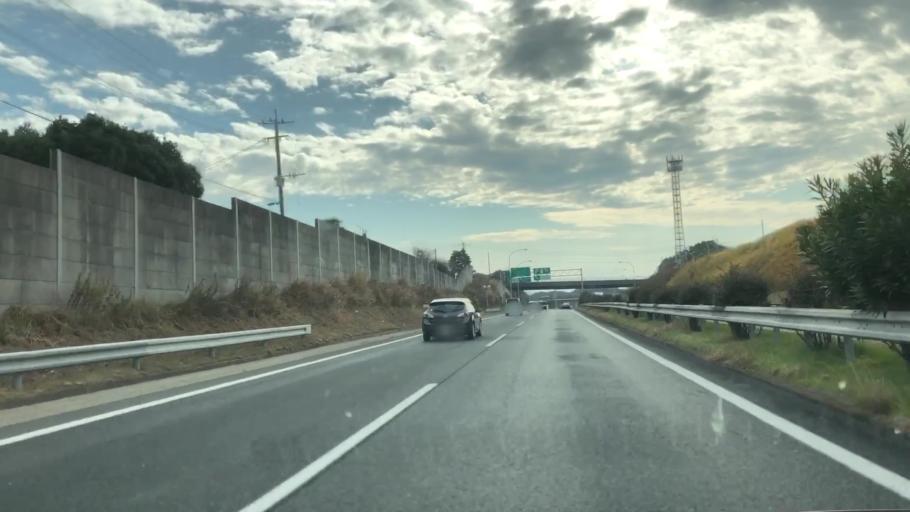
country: JP
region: Fukuoka
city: Kurume
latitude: 33.2595
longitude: 130.5380
